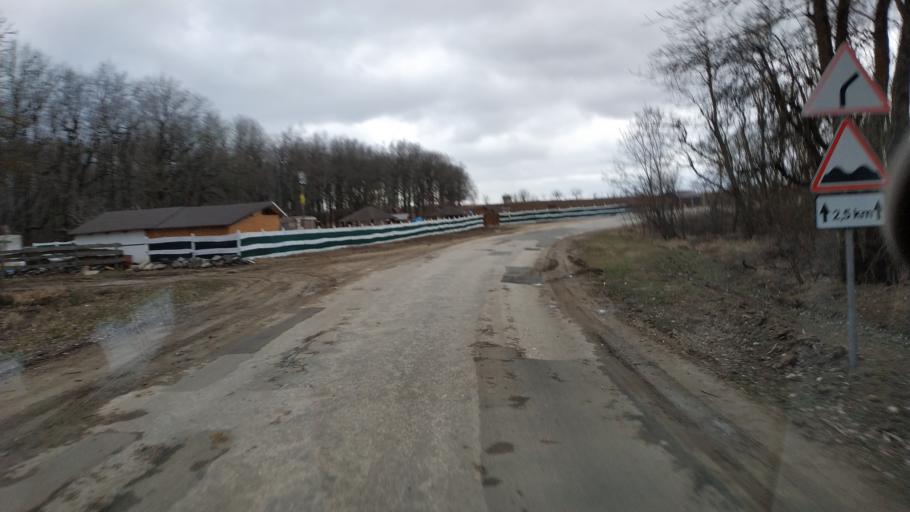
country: MD
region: Calarasi
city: Calarasi
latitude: 47.2214
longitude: 28.2731
